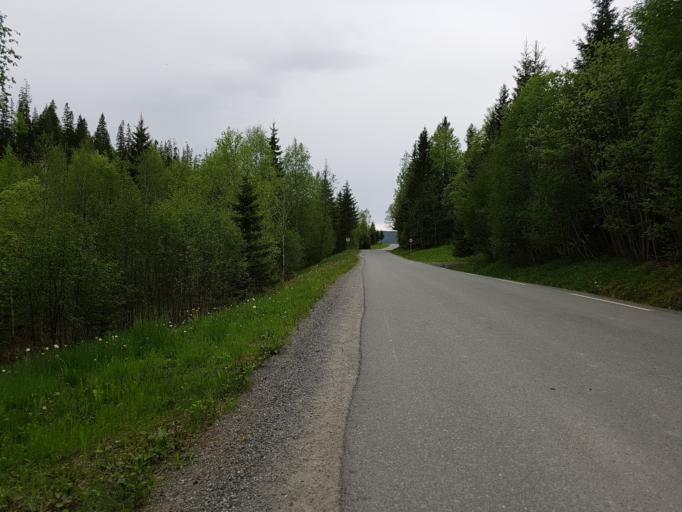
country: NO
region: Nord-Trondelag
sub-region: Levanger
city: Skogn
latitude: 63.6296
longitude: 11.2770
